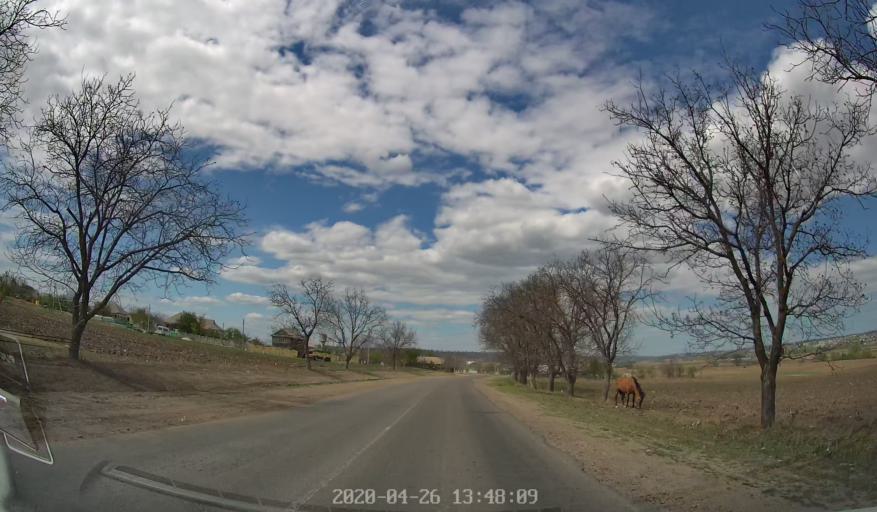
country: MD
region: Telenesti
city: Dubasari
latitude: 47.2446
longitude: 29.1422
